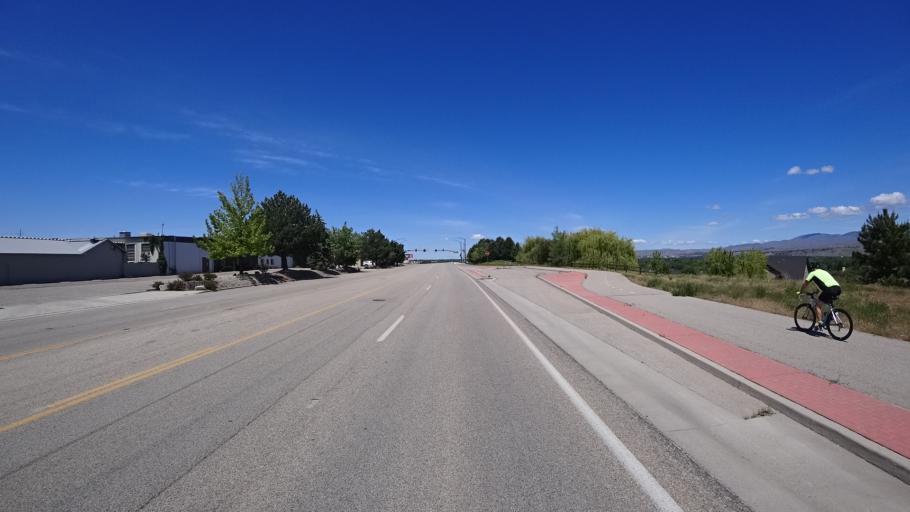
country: US
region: Idaho
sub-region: Ada County
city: Boise
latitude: 43.5623
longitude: -116.1713
